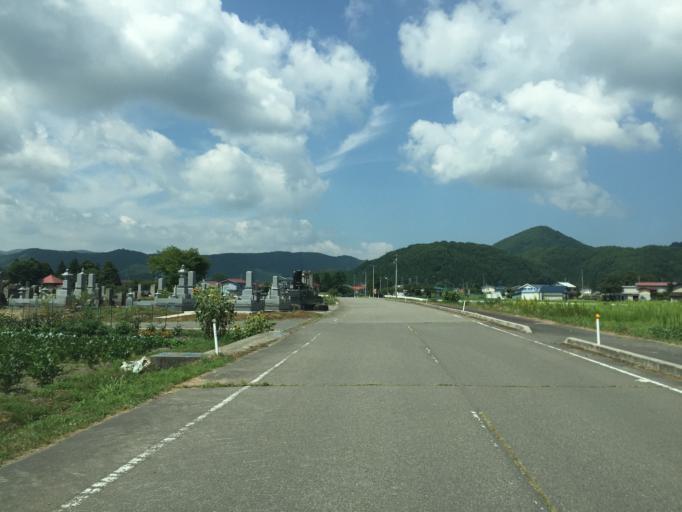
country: JP
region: Fukushima
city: Inawashiro
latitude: 37.4174
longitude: 140.0862
